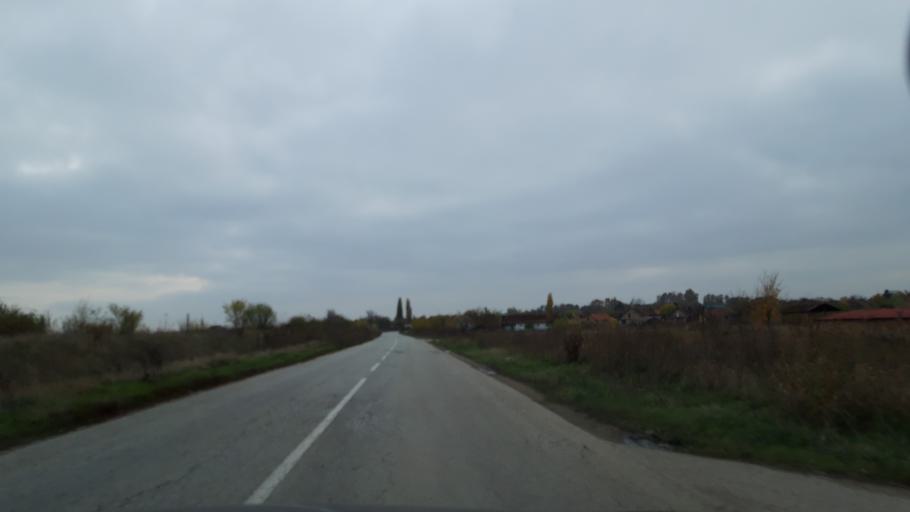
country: RS
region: Autonomna Pokrajina Vojvodina
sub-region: Severnobanatski Okrug
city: Novi Knezevac
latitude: 46.0490
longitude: 20.1038
